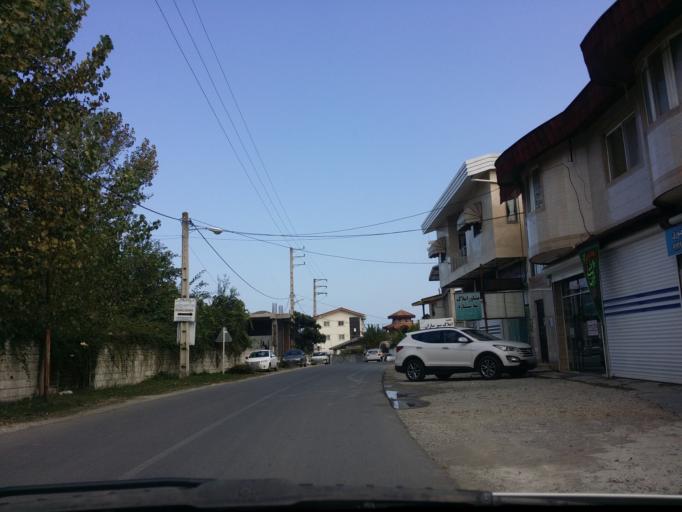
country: IR
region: Mazandaran
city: Chalus
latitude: 36.6679
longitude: 51.3626
